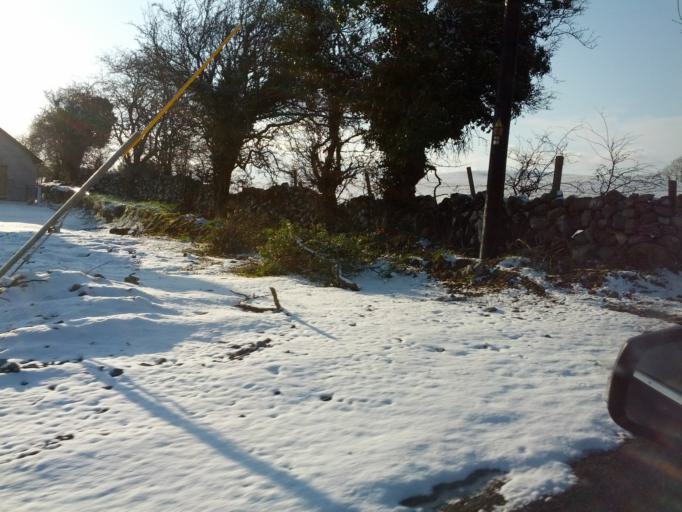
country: IE
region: Connaught
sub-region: County Galway
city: Athenry
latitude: 53.1942
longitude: -8.7343
